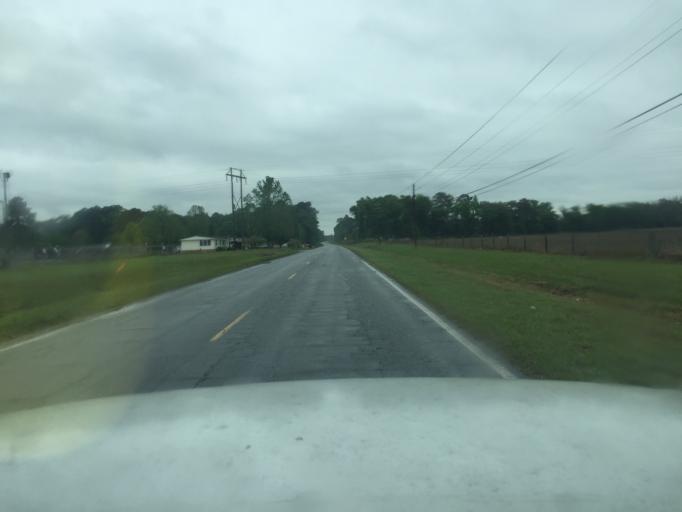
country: US
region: Georgia
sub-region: Chatham County
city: Georgetown
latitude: 32.0085
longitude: -81.2524
